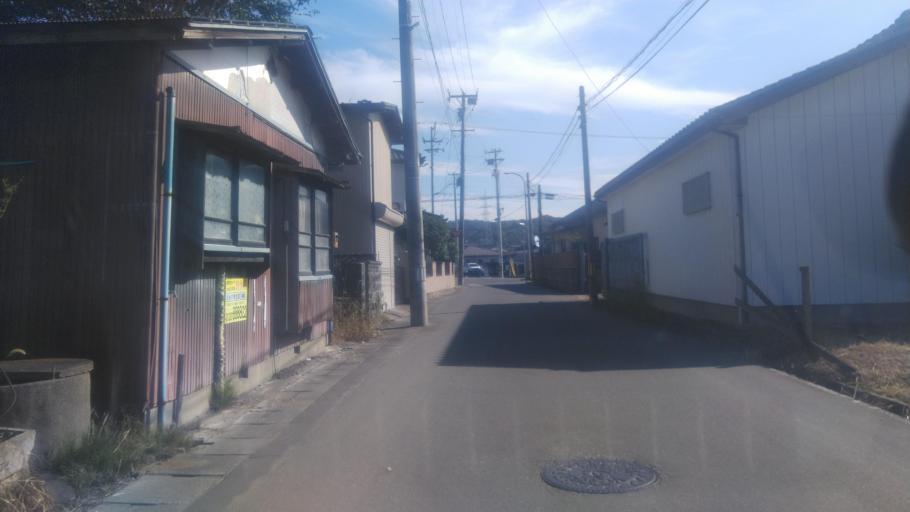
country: JP
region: Miyagi
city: Okawara
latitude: 38.0437
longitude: 140.7064
